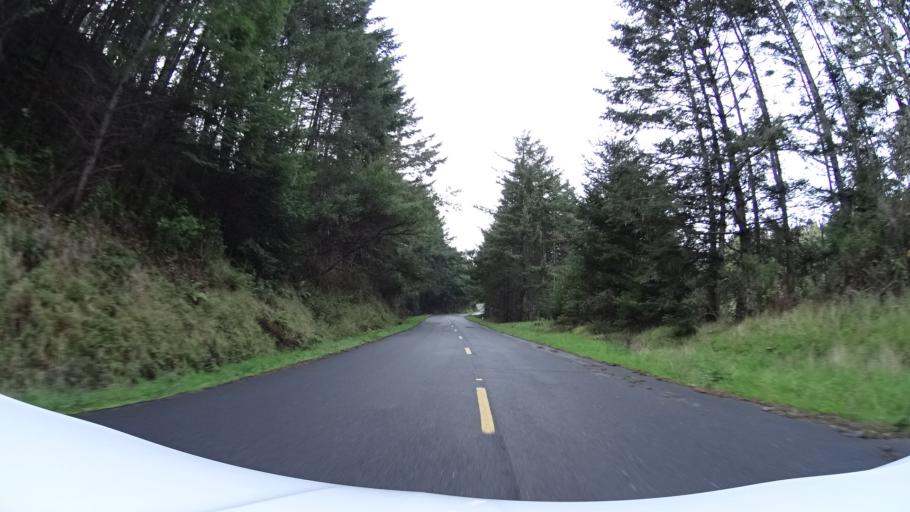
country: US
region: California
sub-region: Humboldt County
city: Ferndale
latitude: 40.3460
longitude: -124.3497
